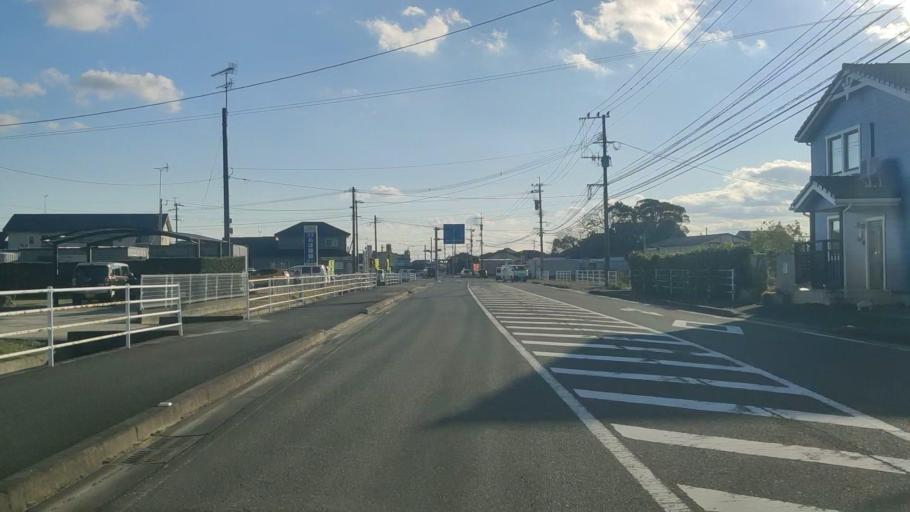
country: JP
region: Saga Prefecture
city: Saga-shi
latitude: 33.3109
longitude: 130.2648
